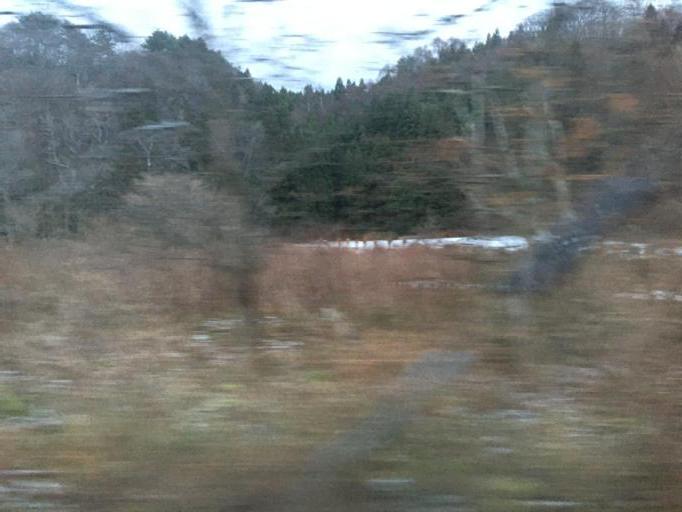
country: JP
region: Aomori
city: Aomori Shi
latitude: 40.8127
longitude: 140.6456
